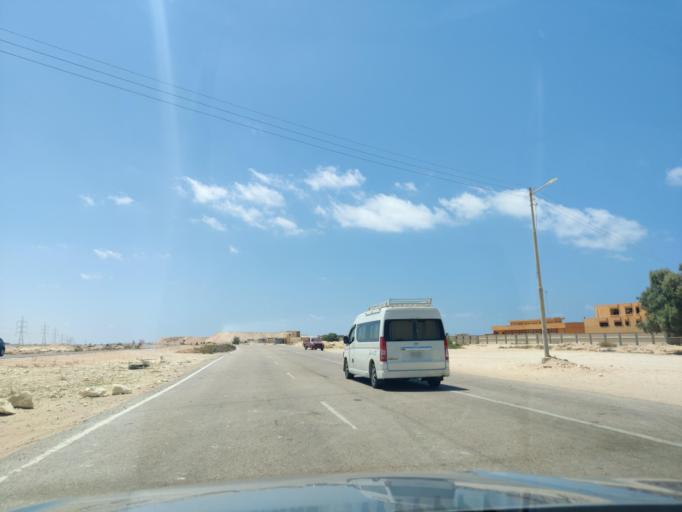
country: EG
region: Muhafazat Matruh
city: Al `Alamayn
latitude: 31.0629
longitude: 28.1993
